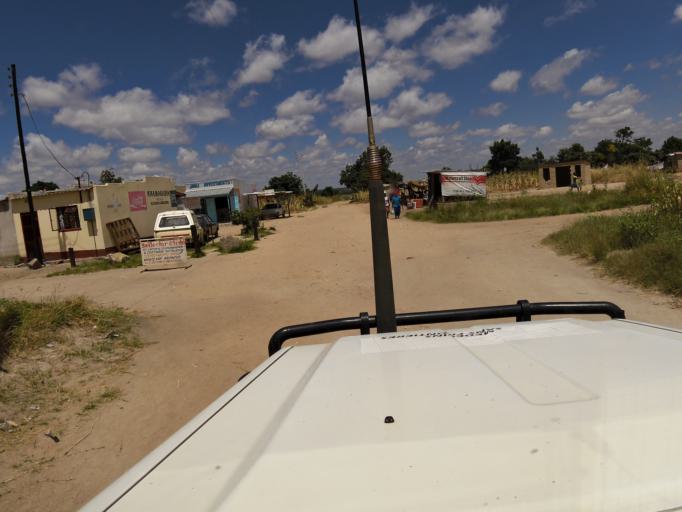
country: ZW
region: Harare
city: Epworth
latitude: -17.9050
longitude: 31.1549
